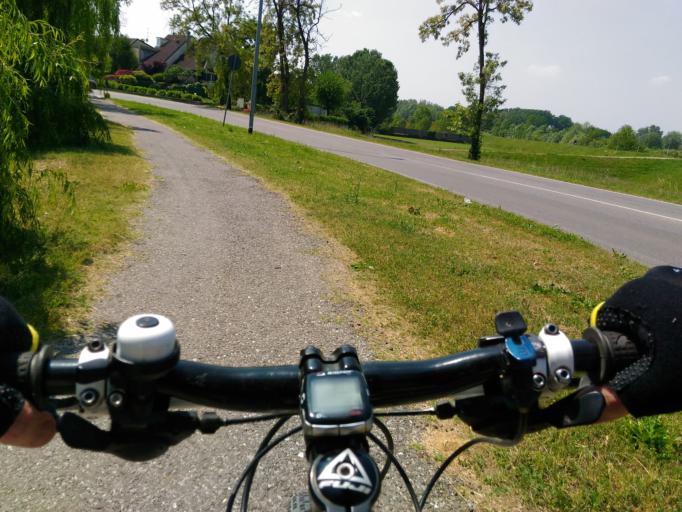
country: IT
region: Lombardy
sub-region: Provincia di Lodi
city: Lodi
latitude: 45.3239
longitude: 9.5109
